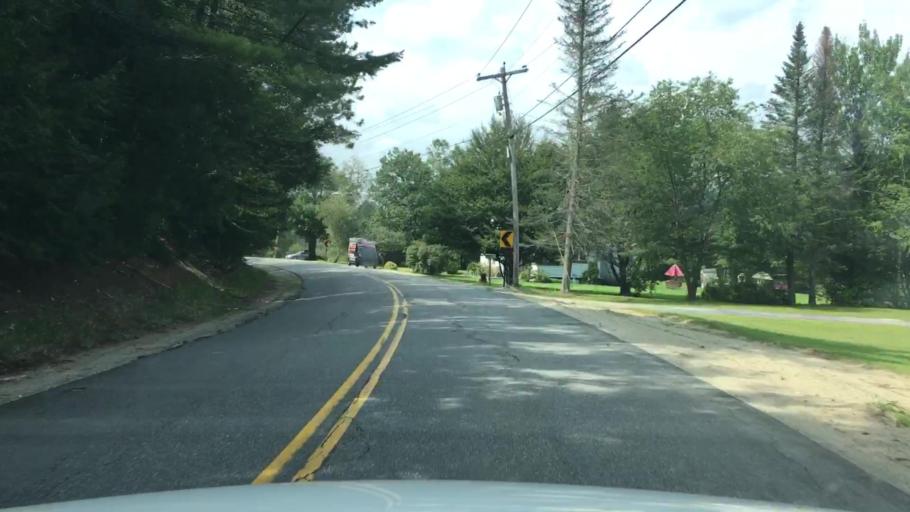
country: US
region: Maine
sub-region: Oxford County
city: Rumford
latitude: 44.5347
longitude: -70.6444
